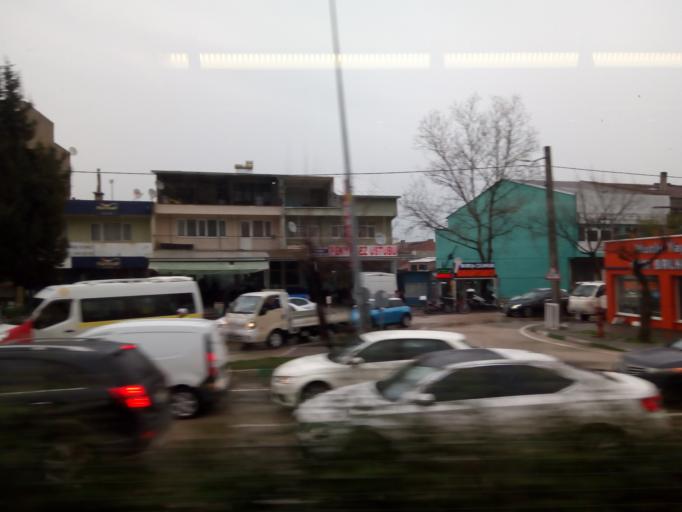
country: TR
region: Bursa
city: Yildirim
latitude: 40.2033
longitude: 29.0335
